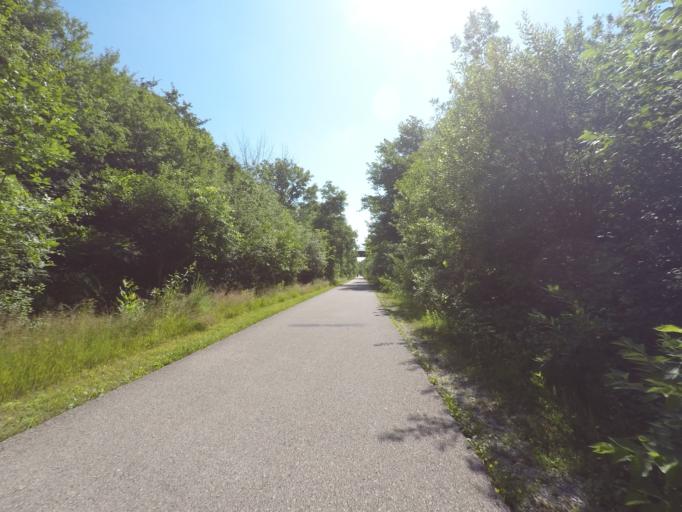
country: US
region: Wisconsin
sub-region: Milwaukee County
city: West Allis
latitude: 43.0245
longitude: -88.0013
